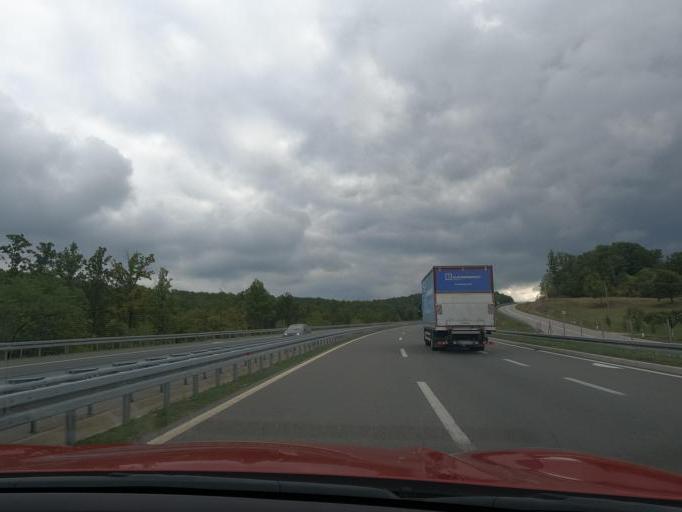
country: RS
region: Central Serbia
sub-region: Moravicki Okrug
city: Gornji Milanovac
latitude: 44.1123
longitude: 20.3822
